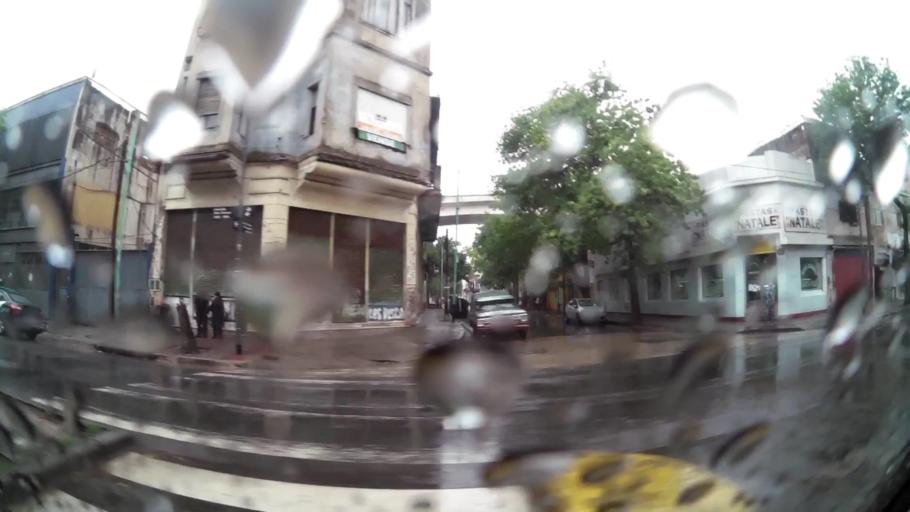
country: AR
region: Buenos Aires
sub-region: Partido de Avellaneda
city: Avellaneda
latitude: -34.6370
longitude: -58.3578
